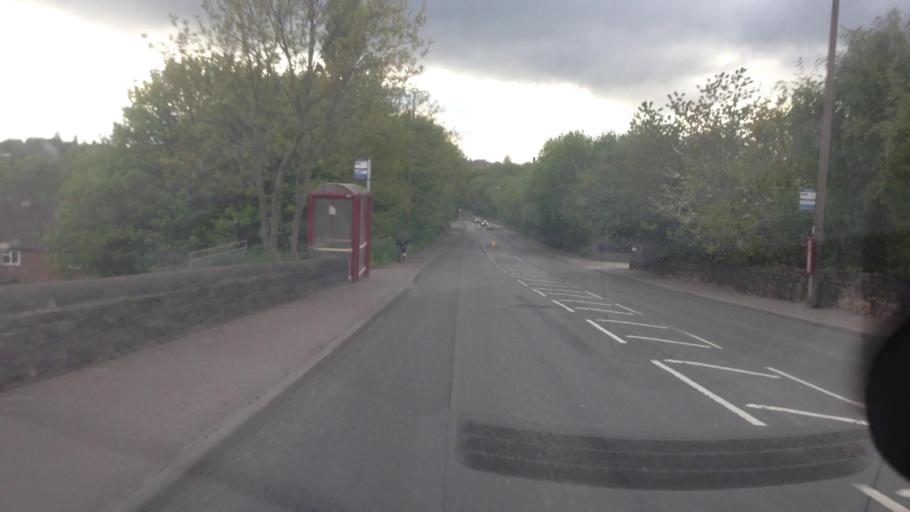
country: GB
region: England
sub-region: City and Borough of Wakefield
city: Ossett
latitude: 53.6918
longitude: -1.5992
